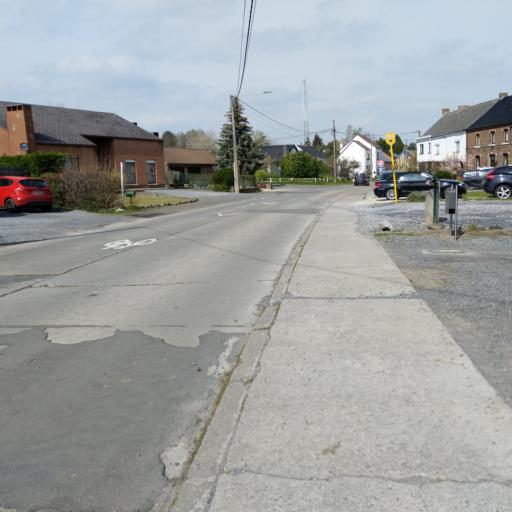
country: BE
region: Wallonia
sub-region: Province du Hainaut
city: Chasse Royale
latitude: 50.4312
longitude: 3.9589
